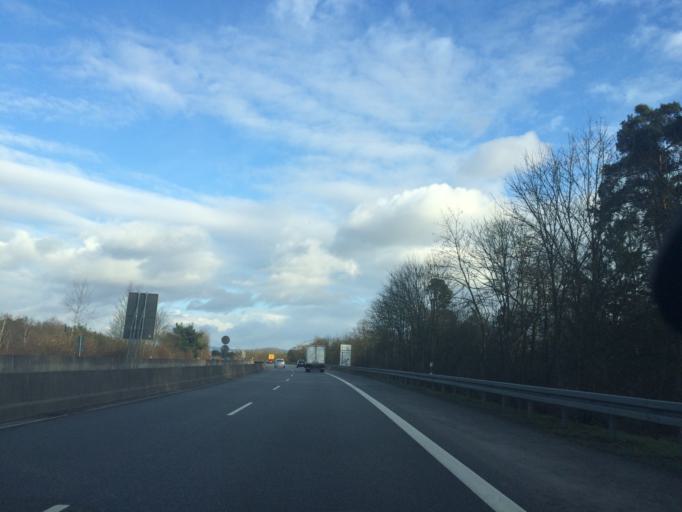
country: DE
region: Hesse
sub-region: Regierungsbezirk Darmstadt
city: Einhausen
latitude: 49.6503
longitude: 8.5339
